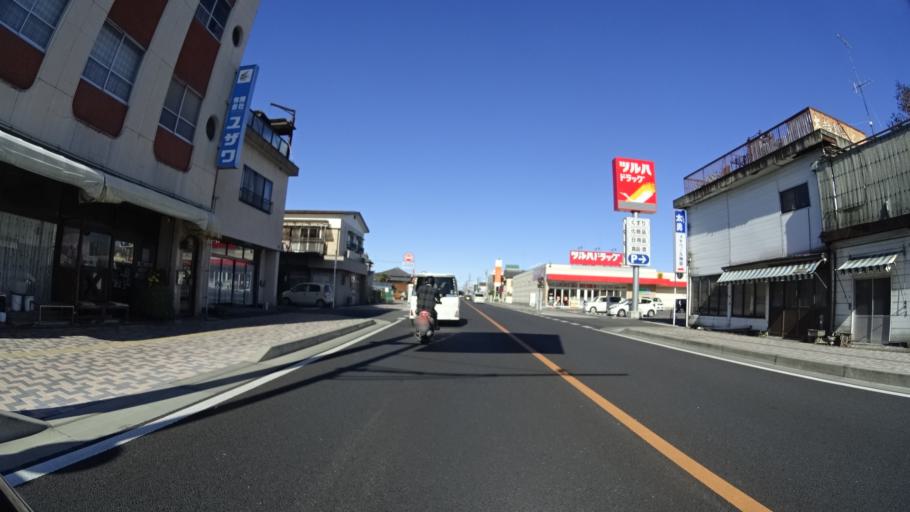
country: JP
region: Tochigi
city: Tochigi
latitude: 36.3919
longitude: 139.7365
